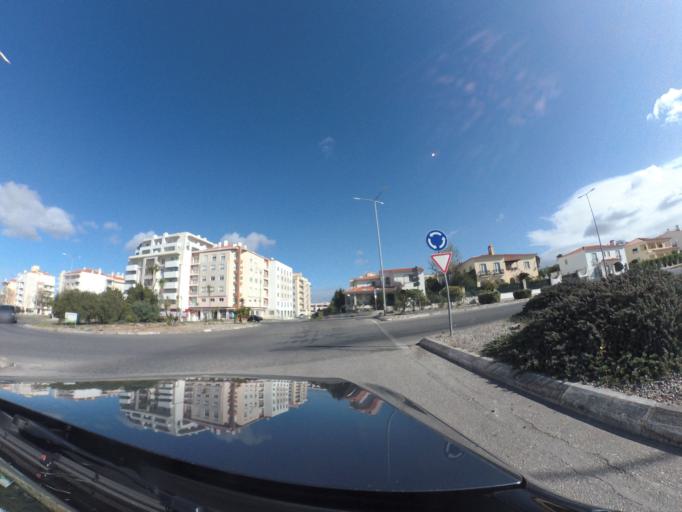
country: PT
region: Leiria
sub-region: Caldas da Rainha
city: Caldas da Rainha
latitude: 39.4126
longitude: -9.1364
